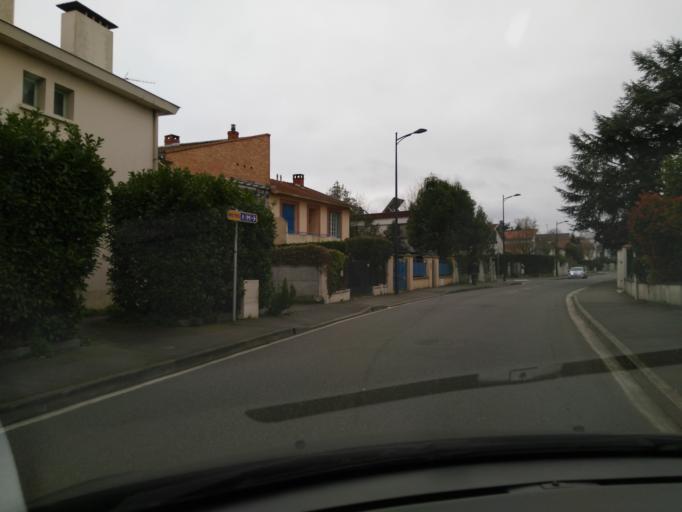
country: FR
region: Midi-Pyrenees
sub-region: Departement de la Haute-Garonne
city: Ramonville-Saint-Agne
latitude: 43.5756
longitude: 1.4601
